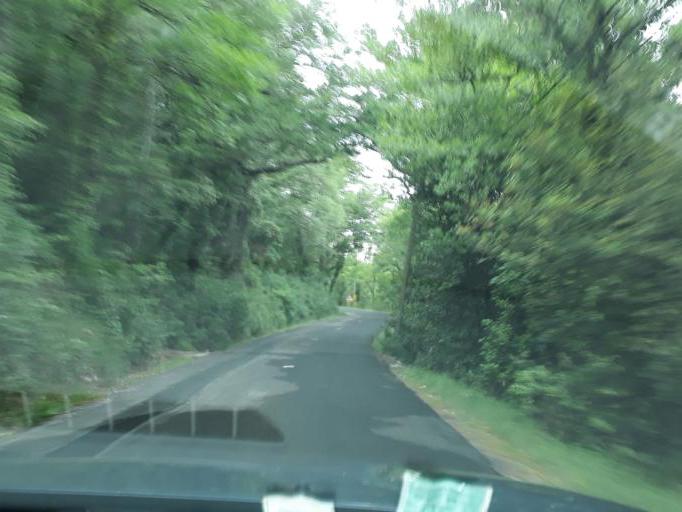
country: FR
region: Languedoc-Roussillon
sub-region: Departement de l'Herault
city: Lodeve
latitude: 43.7621
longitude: 3.3175
